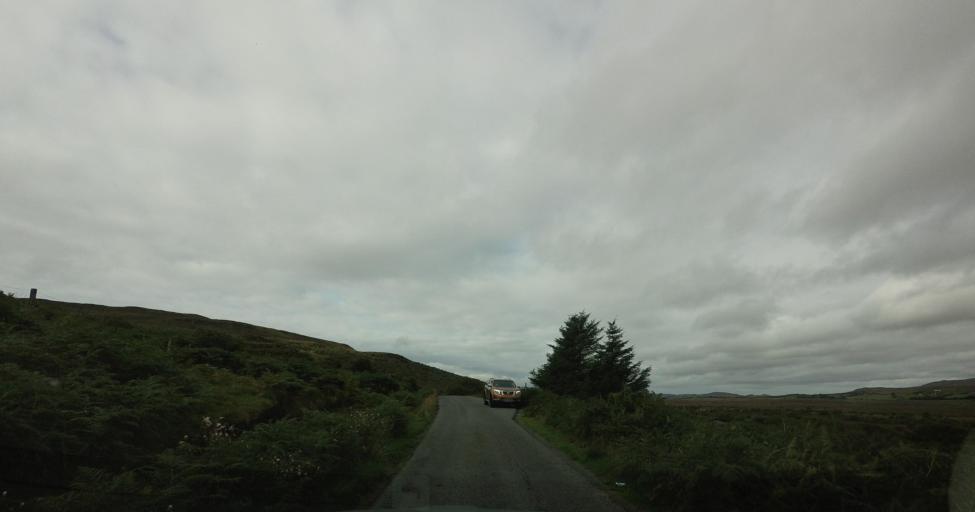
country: GB
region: Scotland
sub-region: Highland
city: Portree
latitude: 57.4169
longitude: -6.2279
